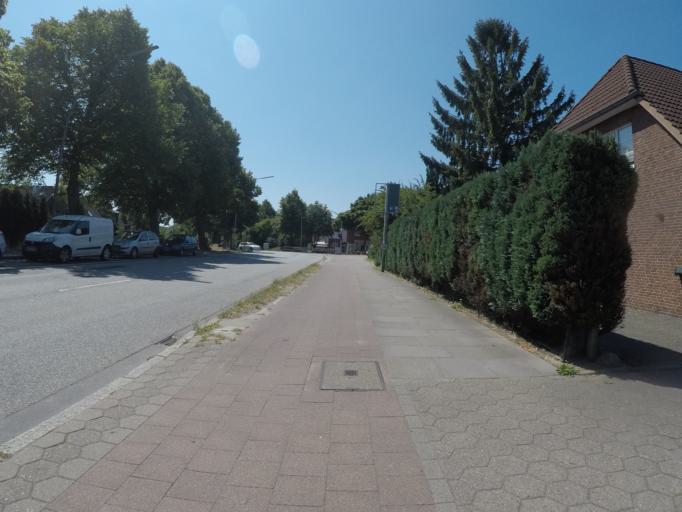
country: DE
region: Hamburg
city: Kleiner Grasbrook
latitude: 53.4920
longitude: 10.0187
